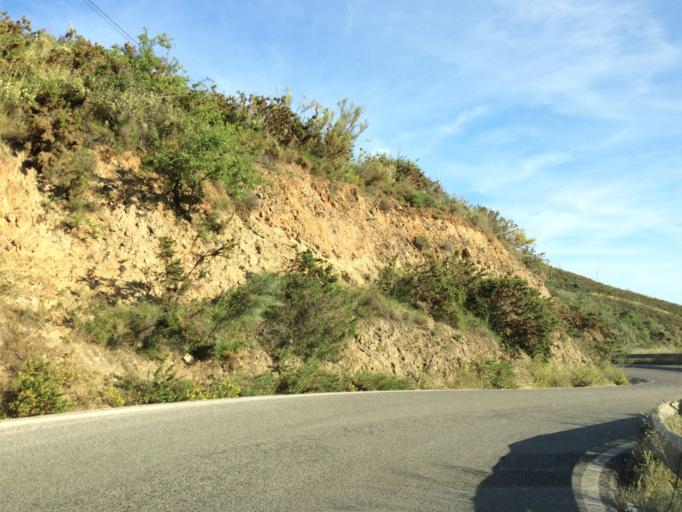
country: ES
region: Andalusia
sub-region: Provincia de Malaga
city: Totalan
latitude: 36.7448
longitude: -4.3293
